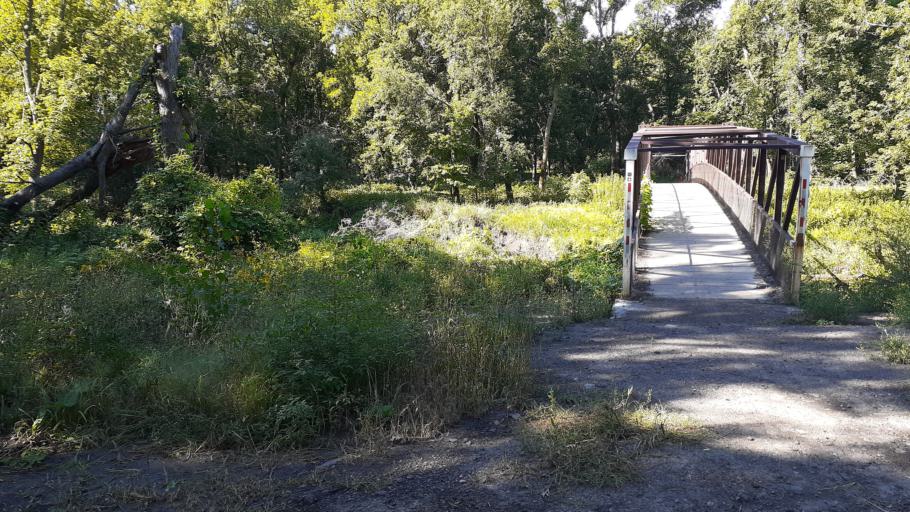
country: US
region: Minnesota
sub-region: Clay County
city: Oakport
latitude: 46.9097
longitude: -96.7609
